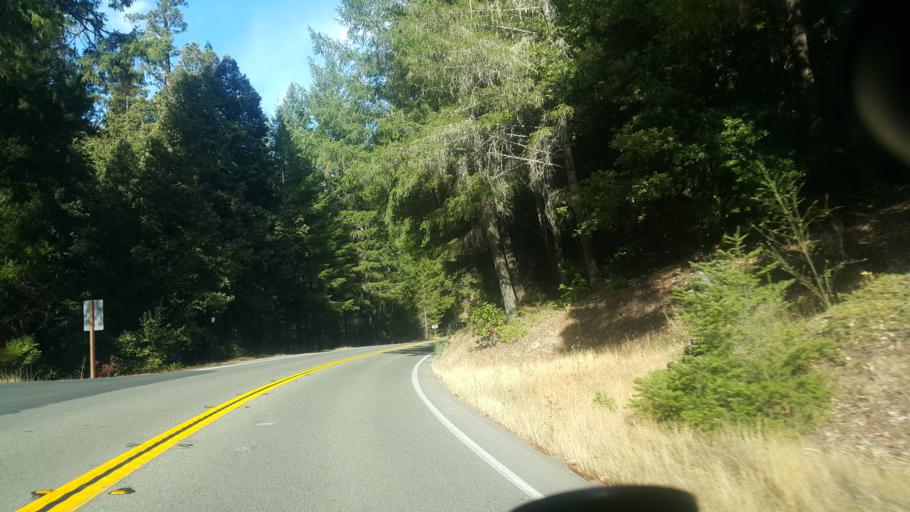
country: US
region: California
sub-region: Mendocino County
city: Brooktrails
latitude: 39.3481
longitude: -123.5138
